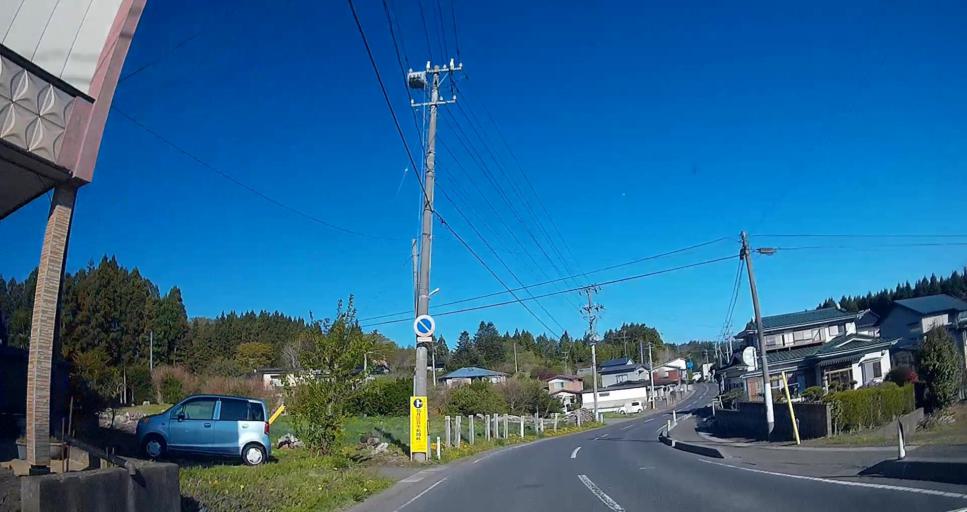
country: JP
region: Aomori
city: Hachinohe
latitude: 40.5167
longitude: 141.5870
